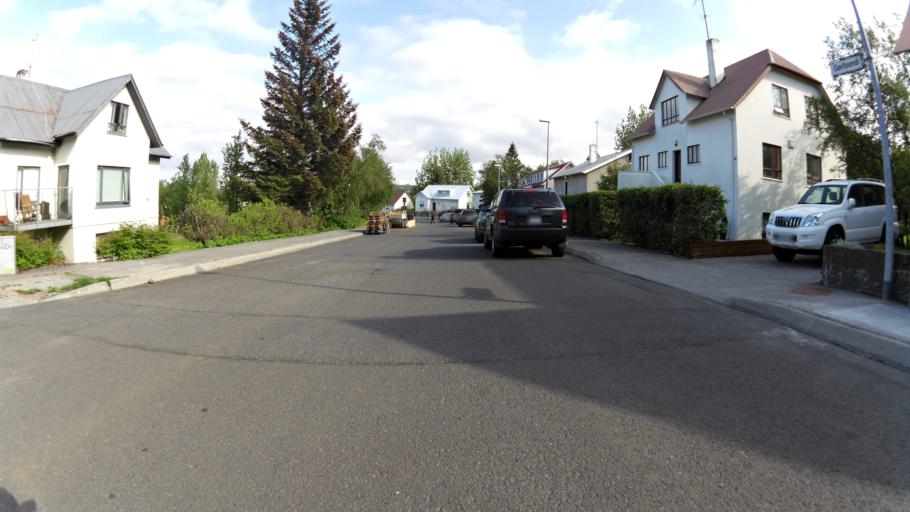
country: IS
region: Capital Region
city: Reykjavik
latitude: 64.1232
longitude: -21.8544
